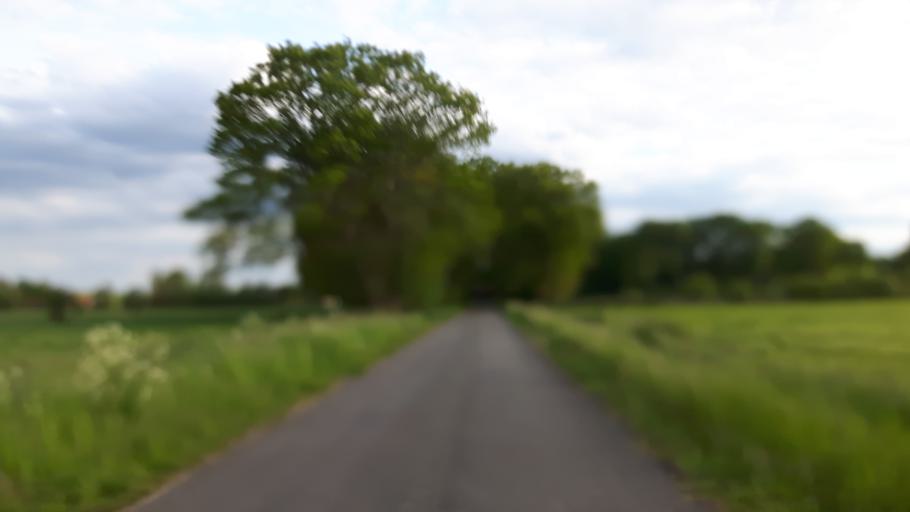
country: DE
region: Lower Saxony
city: Ganderkesee
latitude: 53.0183
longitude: 8.5822
